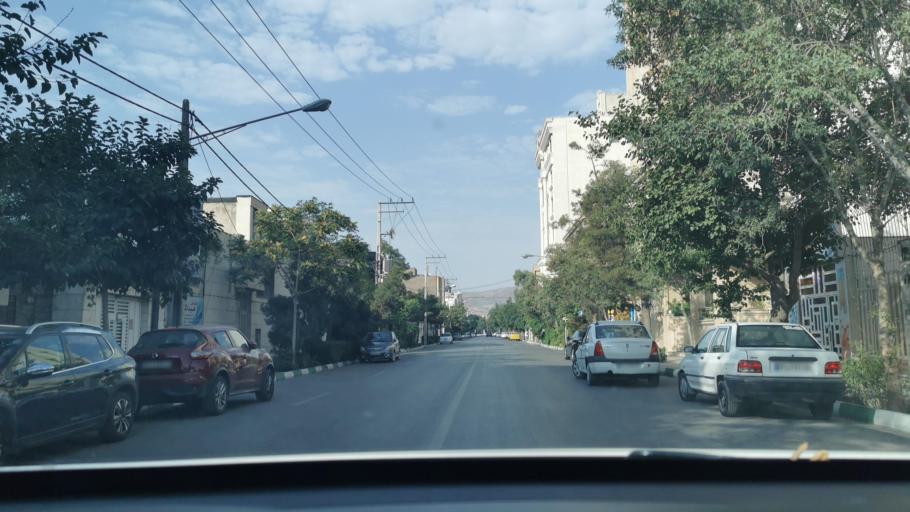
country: IR
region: Razavi Khorasan
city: Mashhad
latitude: 36.3142
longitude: 59.5477
